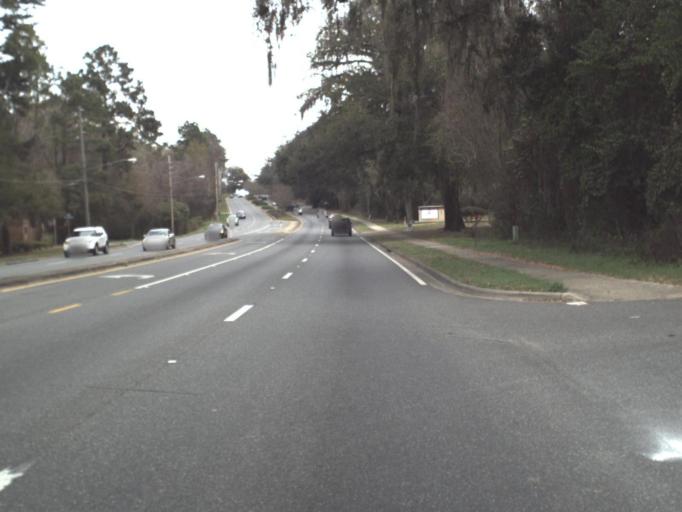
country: US
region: Florida
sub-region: Leon County
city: Tallahassee
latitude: 30.4777
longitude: -84.2612
